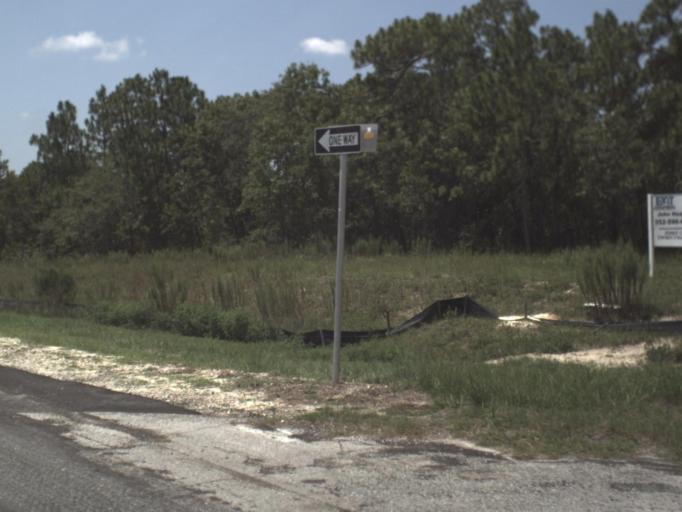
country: US
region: Florida
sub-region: Citrus County
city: Sugarmill Woods
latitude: 28.6829
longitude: -82.5526
